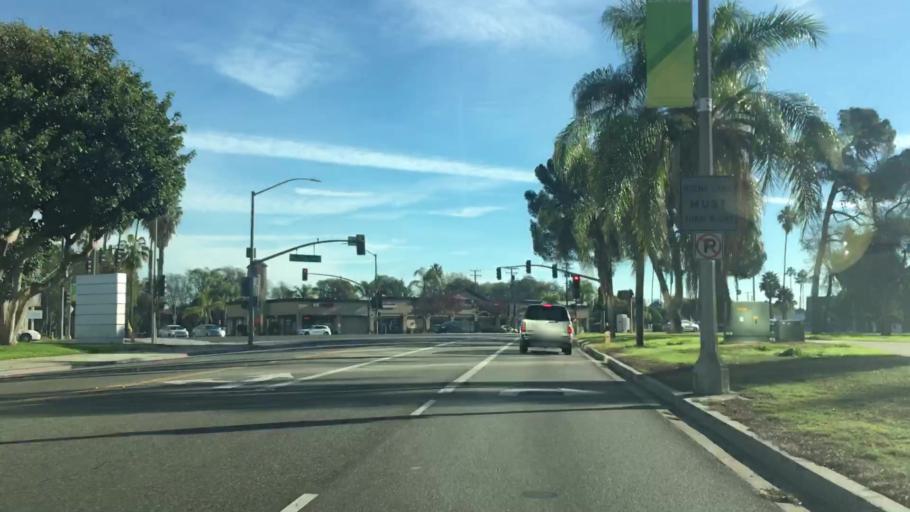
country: US
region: California
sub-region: Los Angeles County
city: Signal Hill
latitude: 33.7825
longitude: -118.1335
